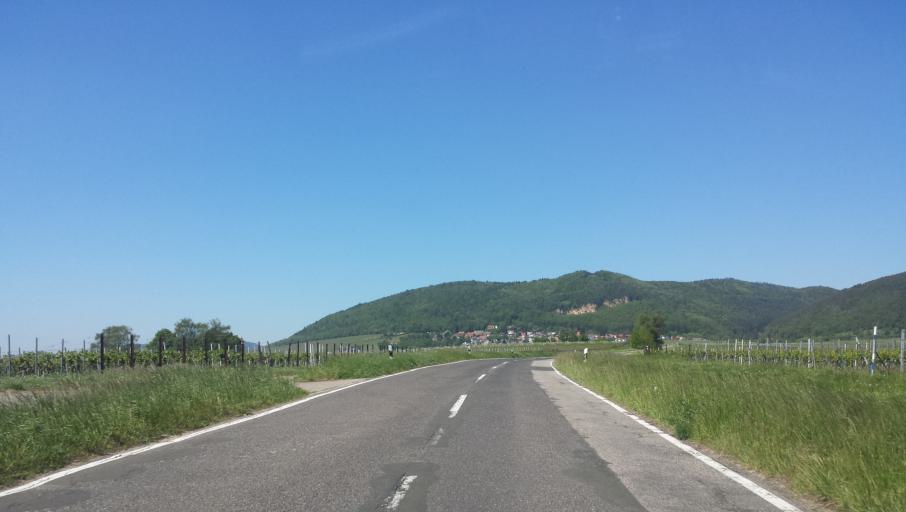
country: DE
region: Rheinland-Pfalz
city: Gleisweiler
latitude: 49.2276
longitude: 8.0781
